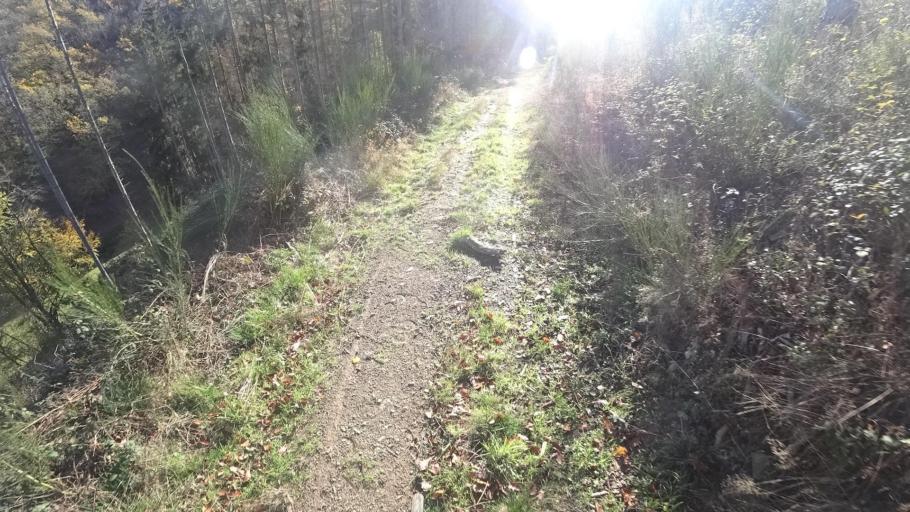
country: DE
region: Rheinland-Pfalz
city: Kirchsahr
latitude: 50.5161
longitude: 6.8955
